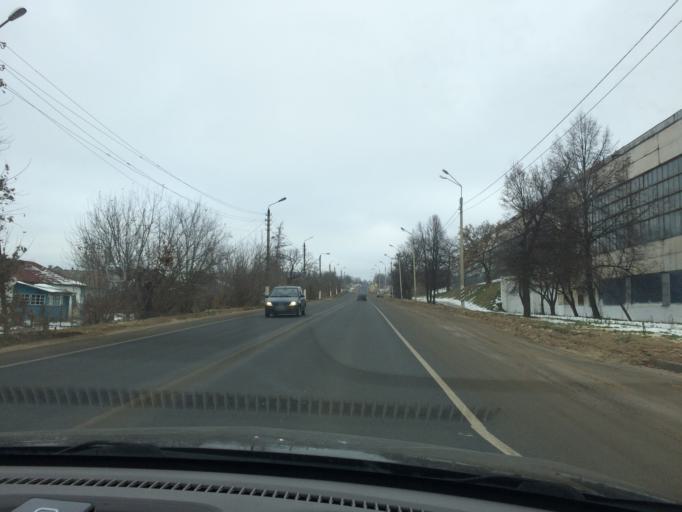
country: RU
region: Tula
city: Plavsk
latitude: 53.7140
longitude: 37.2967
